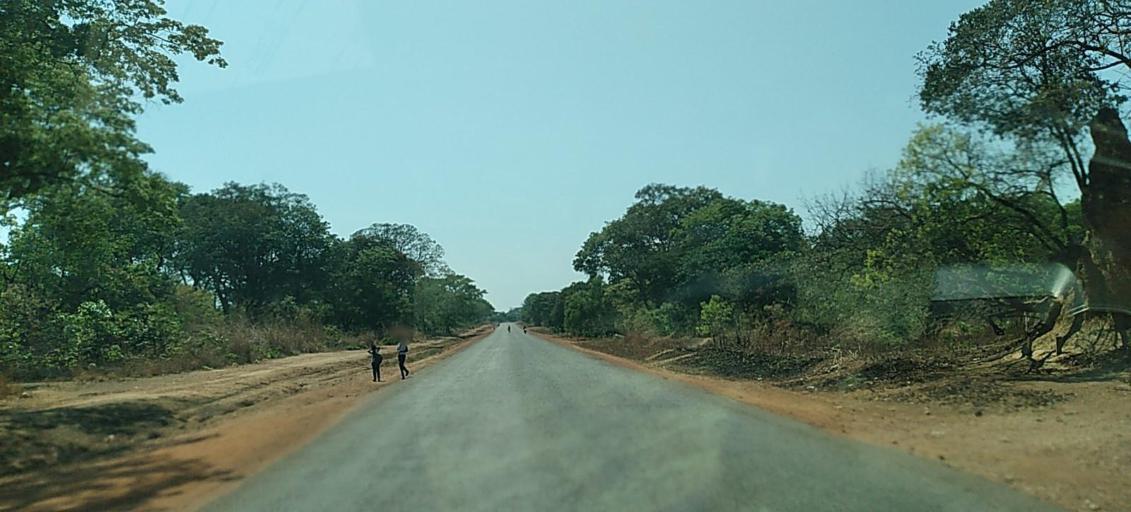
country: ZM
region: North-Western
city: Solwezi
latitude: -12.2747
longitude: 25.6717
